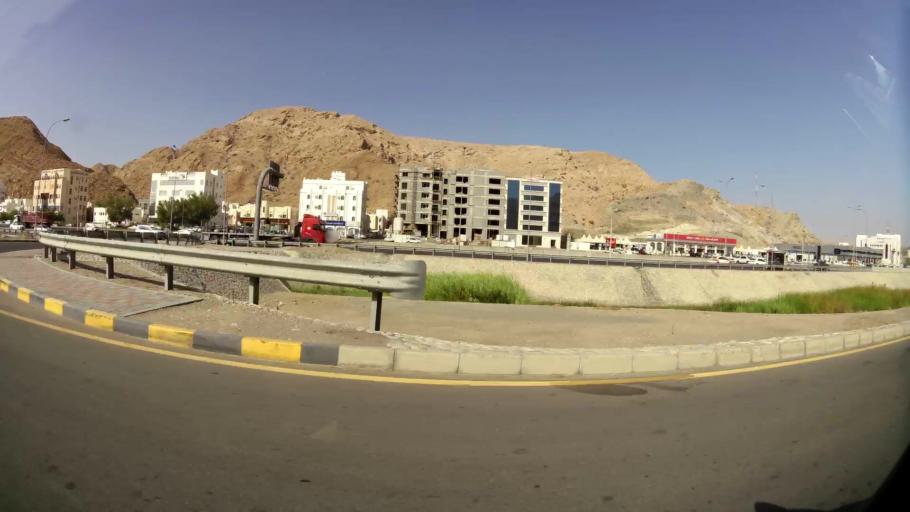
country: OM
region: Muhafazat Masqat
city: Muscat
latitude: 23.5973
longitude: 58.5197
